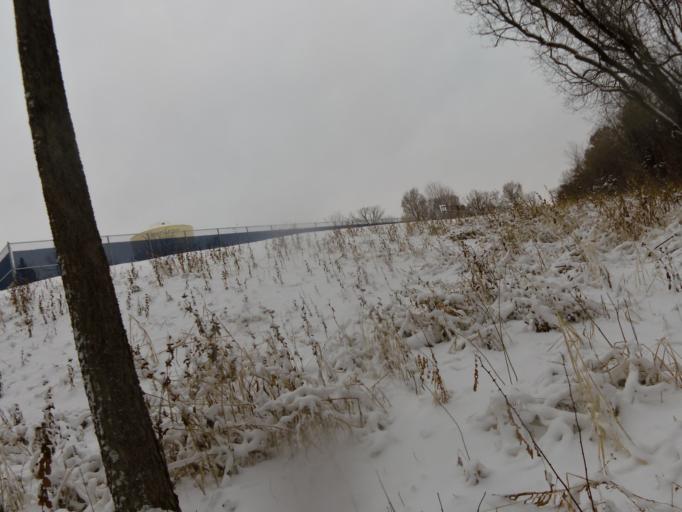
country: US
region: Minnesota
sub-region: Dakota County
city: Inver Grove Heights
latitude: 44.8667
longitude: -93.0739
